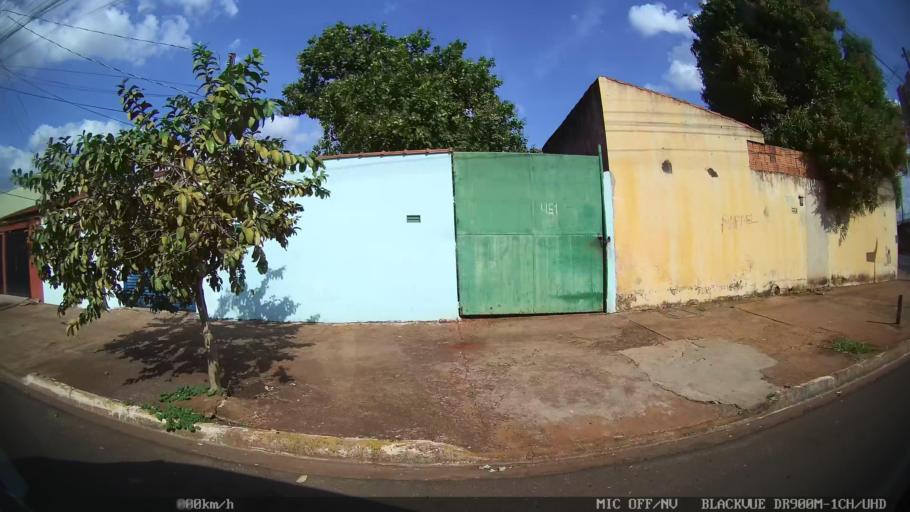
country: BR
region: Sao Paulo
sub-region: Ribeirao Preto
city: Ribeirao Preto
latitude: -21.1799
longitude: -47.8267
